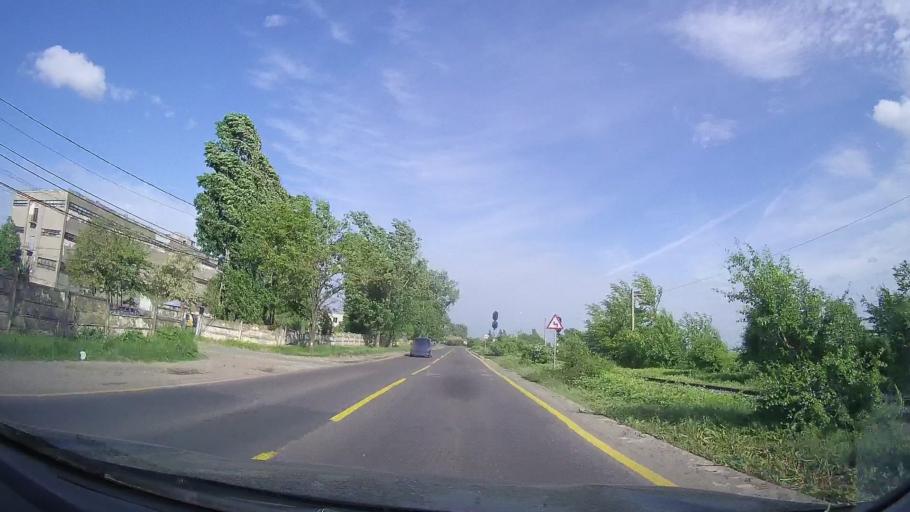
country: RO
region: Ilfov
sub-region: Comuna Magurele
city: Magurele
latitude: 44.3648
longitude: 26.0213
